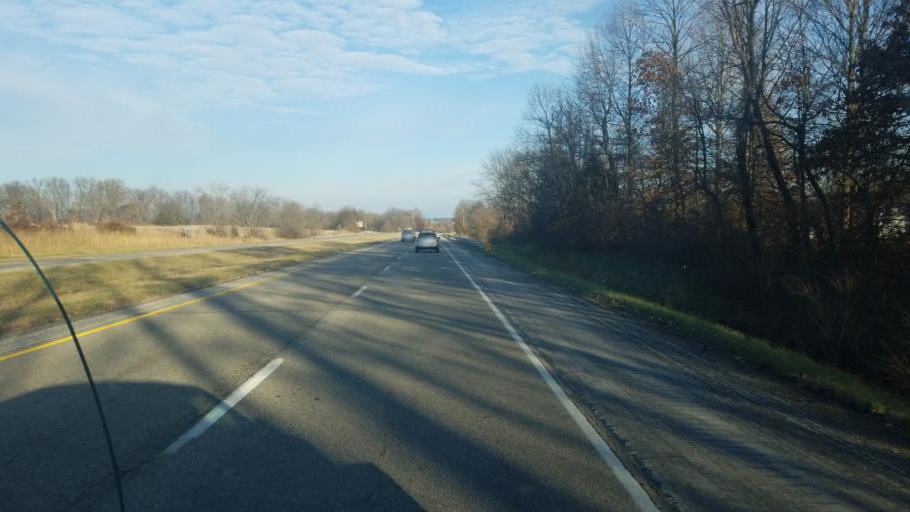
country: US
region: Indiana
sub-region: Knox County
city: Vincennes
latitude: 38.6783
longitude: -87.4173
